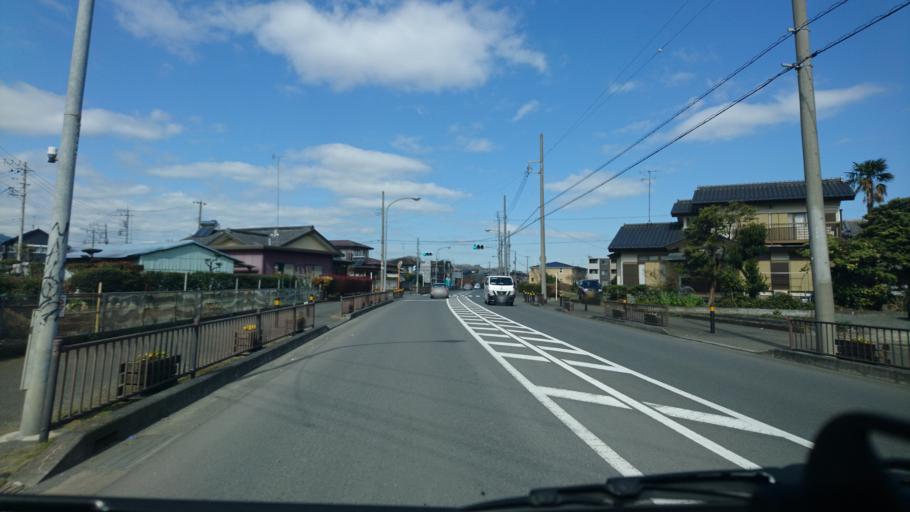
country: JP
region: Kanagawa
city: Zama
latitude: 35.5286
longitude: 139.3353
